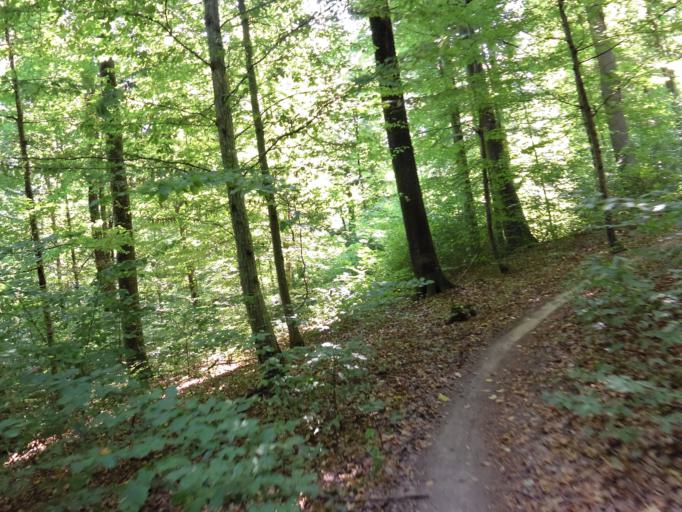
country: DE
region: Bavaria
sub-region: Regierungsbezirk Unterfranken
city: Wuerzburg
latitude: 49.7550
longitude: 9.8829
